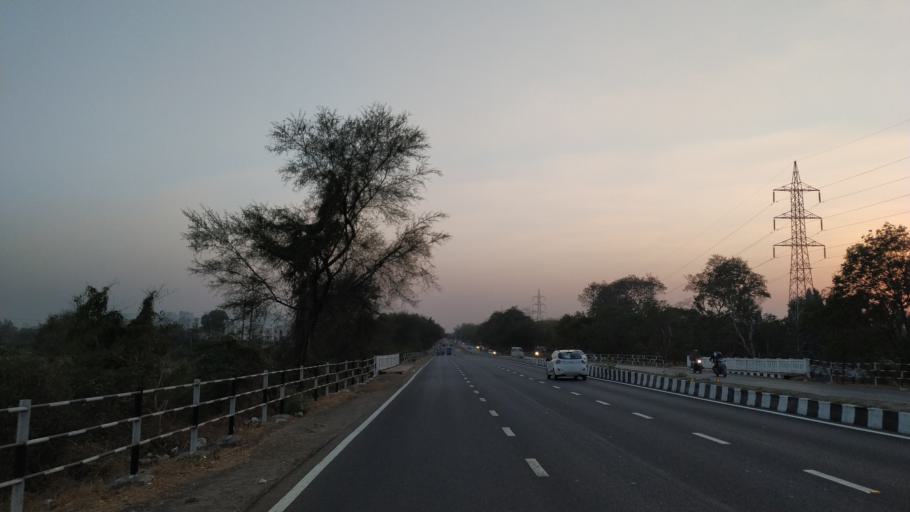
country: IN
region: Gujarat
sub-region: Gandhinagar
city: Adalaj
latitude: 23.1268
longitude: 72.6243
